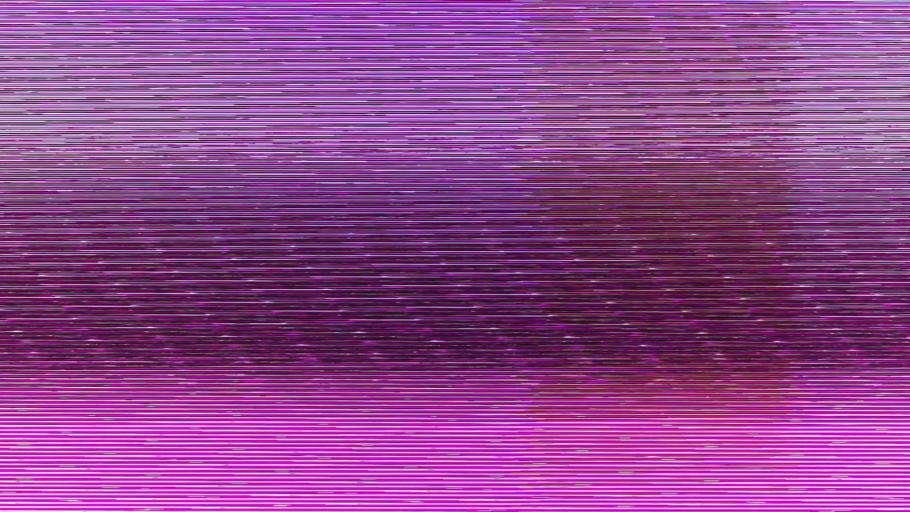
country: US
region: Michigan
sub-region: Genesee County
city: Swartz Creek
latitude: 43.0019
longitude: -83.7908
